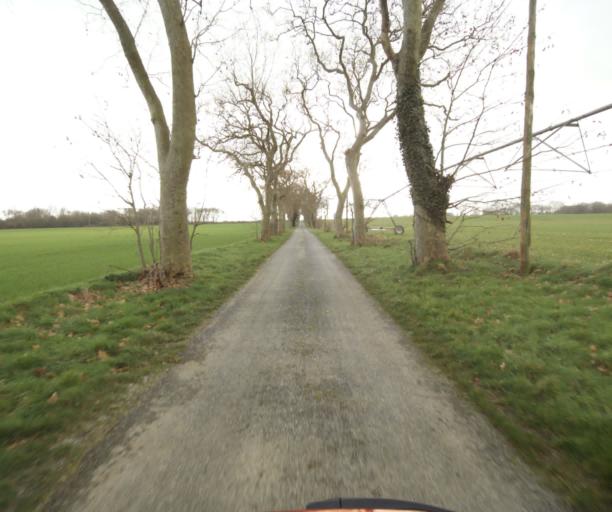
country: FR
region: Midi-Pyrenees
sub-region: Departement de l'Ariege
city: Mazeres
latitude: 43.2239
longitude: 1.7124
